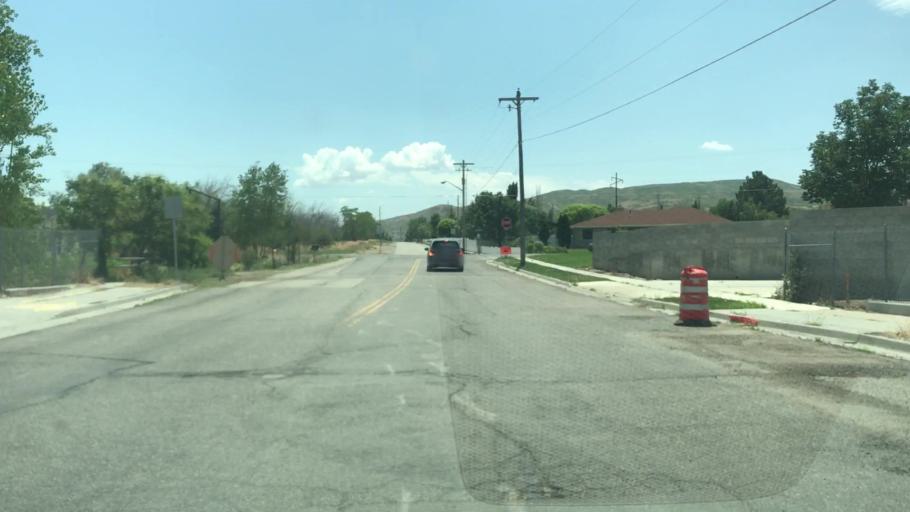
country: US
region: Utah
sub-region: Salt Lake County
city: Bluffdale
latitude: 40.4793
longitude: -111.9484
